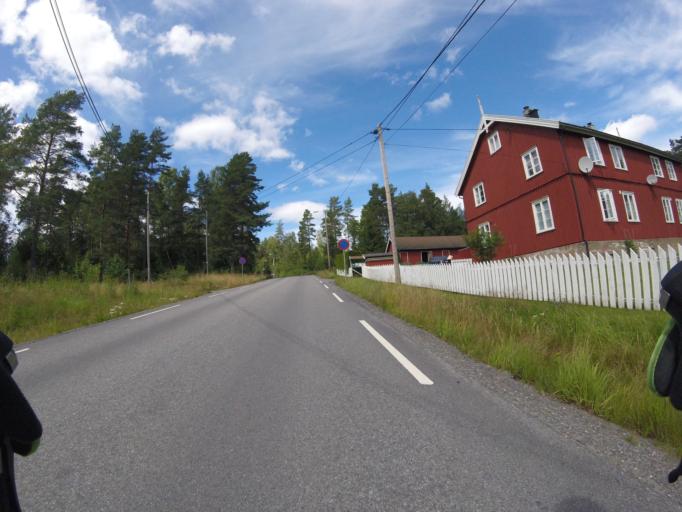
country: NO
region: Akershus
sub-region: Lorenskog
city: Kjenn
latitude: 59.8920
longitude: 10.9774
